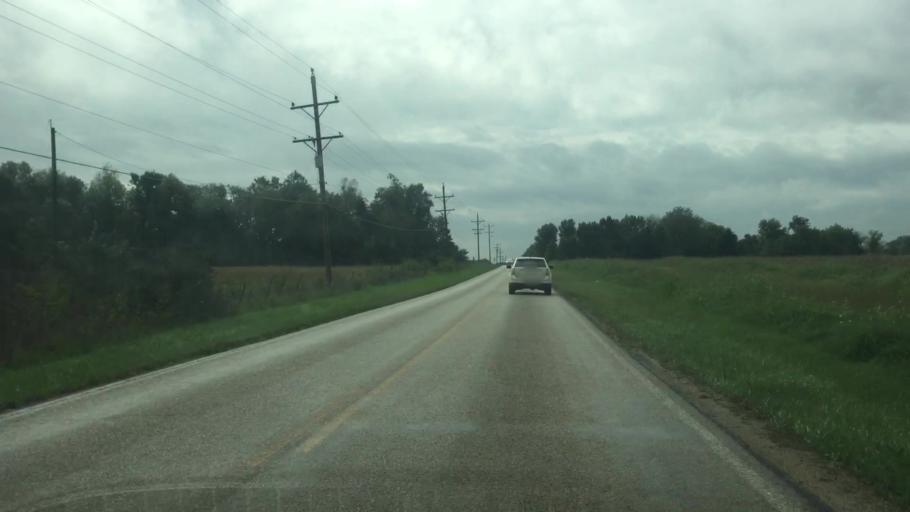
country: US
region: Kansas
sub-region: Allen County
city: Humboldt
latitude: 37.8409
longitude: -95.4368
